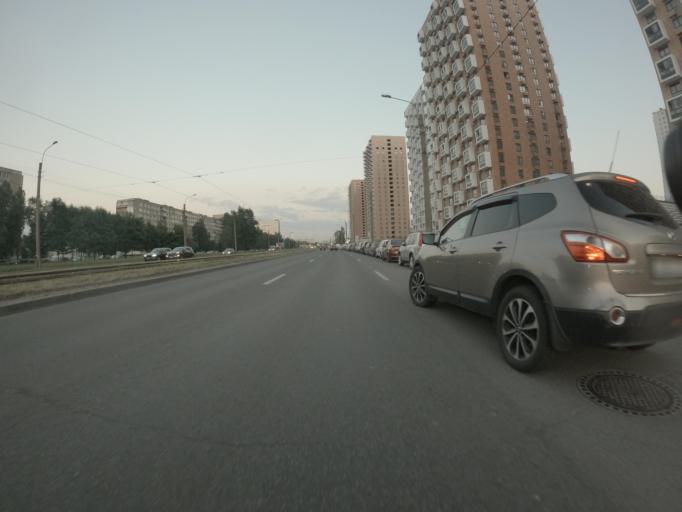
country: RU
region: St.-Petersburg
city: Obukhovo
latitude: 59.8995
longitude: 30.4591
